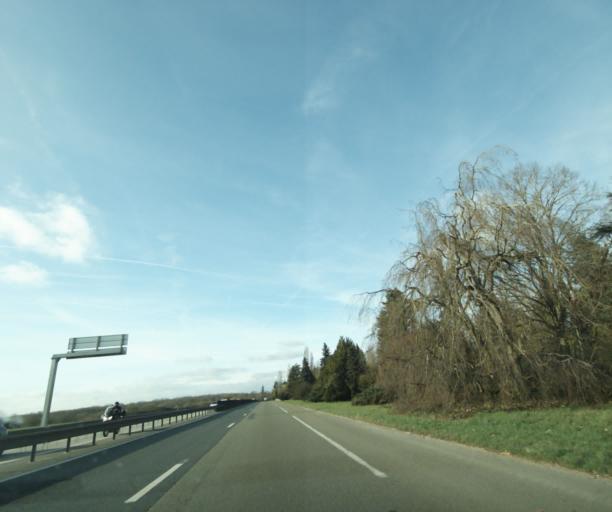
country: FR
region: Ile-de-France
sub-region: Departement des Yvelines
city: Rambouillet
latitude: 48.6571
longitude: 1.8399
